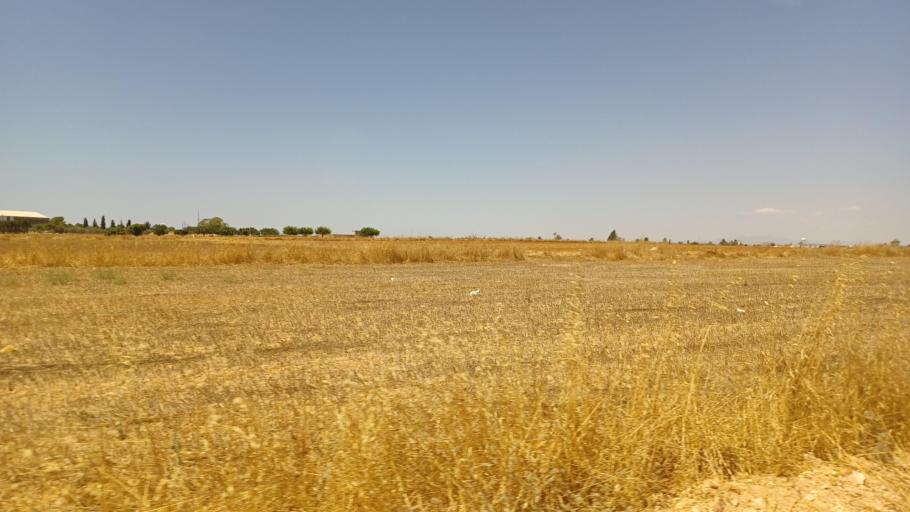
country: CY
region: Larnaka
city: Xylotymbou
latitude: 35.0134
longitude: 33.7269
